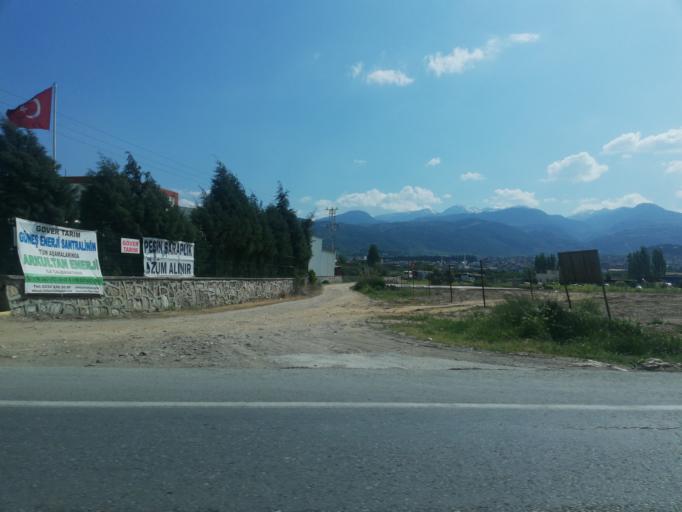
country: TR
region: Manisa
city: Alasehir
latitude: 38.3597
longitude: 28.5327
